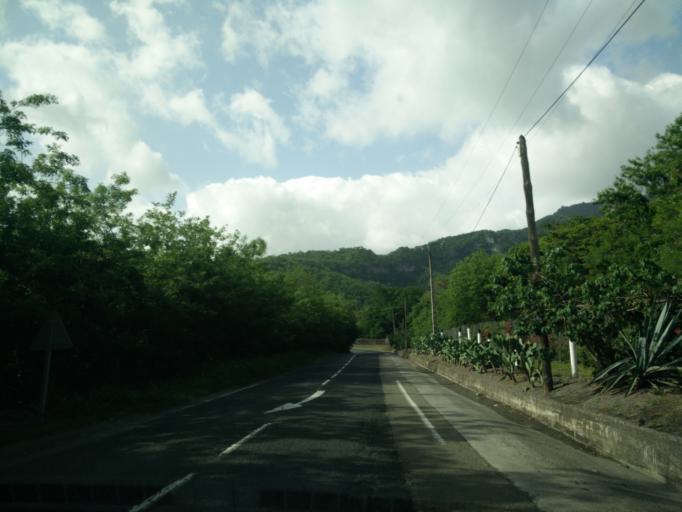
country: MQ
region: Martinique
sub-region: Martinique
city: Saint-Pierre
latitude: 14.7756
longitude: -61.2019
